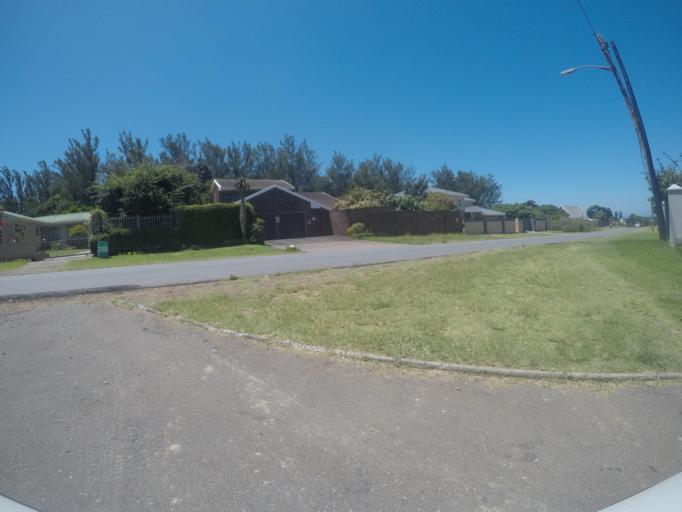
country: ZA
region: Eastern Cape
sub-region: Buffalo City Metropolitan Municipality
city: East London
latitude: -32.9542
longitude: 28.0017
